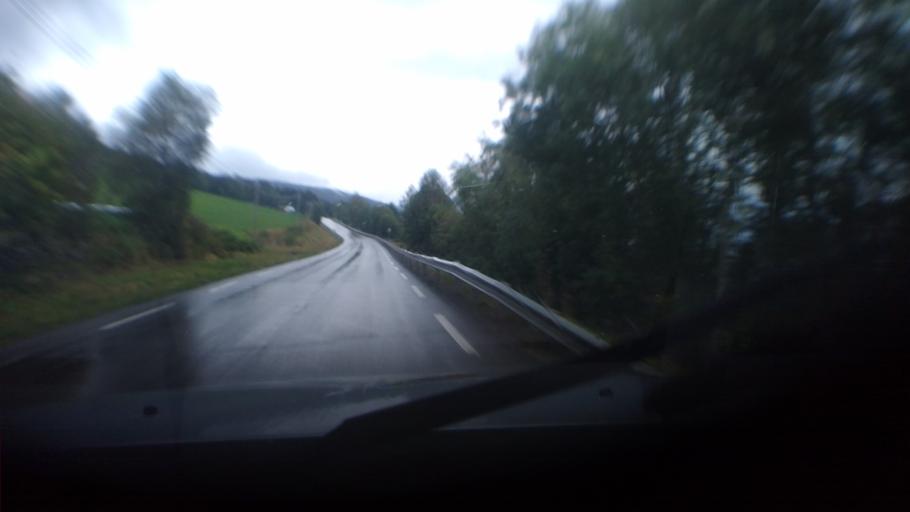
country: NO
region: Oppland
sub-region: Ringebu
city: Ringebu
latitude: 61.5897
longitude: 10.0543
